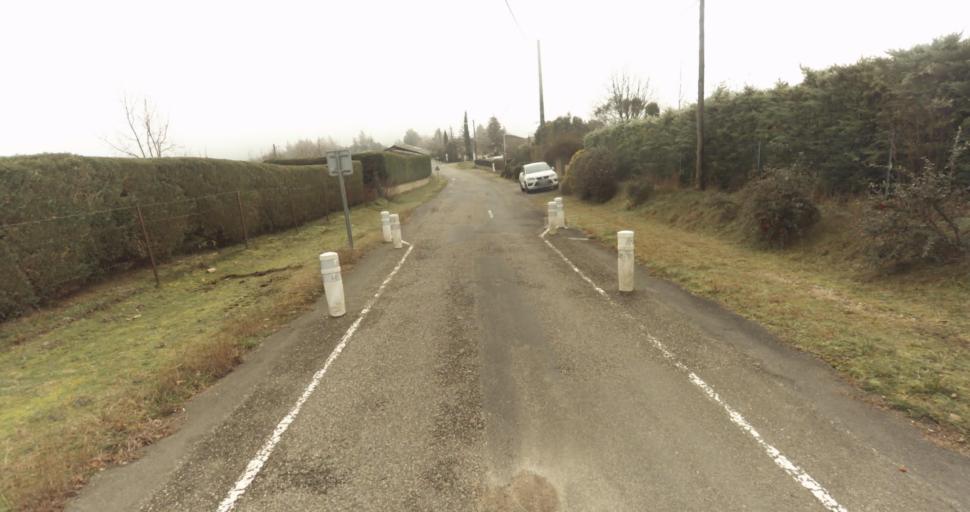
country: FR
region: Midi-Pyrenees
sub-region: Departement du Lot
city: Figeac
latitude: 44.6234
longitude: 2.0225
